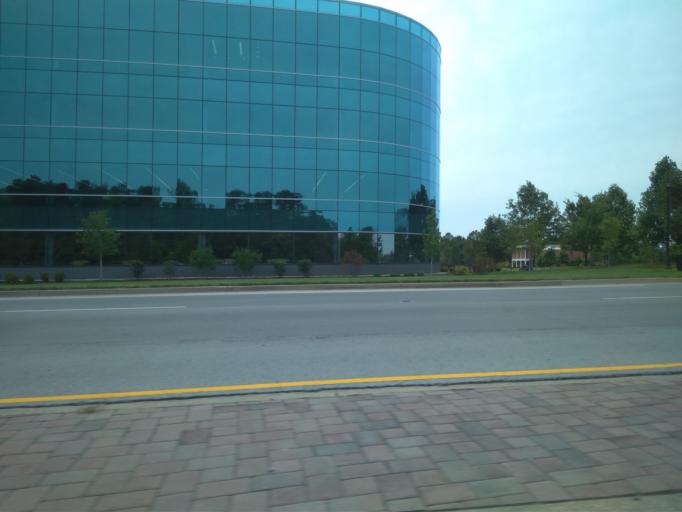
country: US
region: Kentucky
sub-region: Jefferson County
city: Hurstbourne
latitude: 38.2535
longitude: -85.5801
